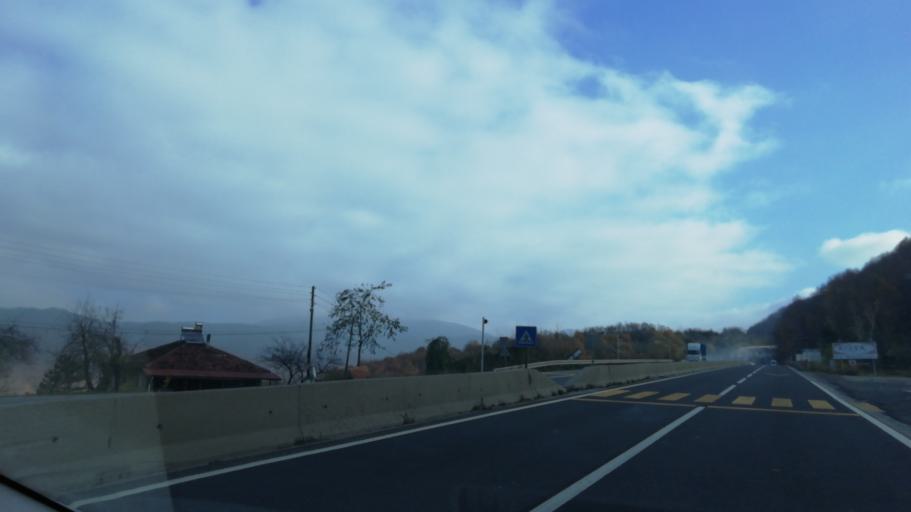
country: TR
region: Duzce
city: Kaynasli
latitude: 40.7582
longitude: 31.3528
